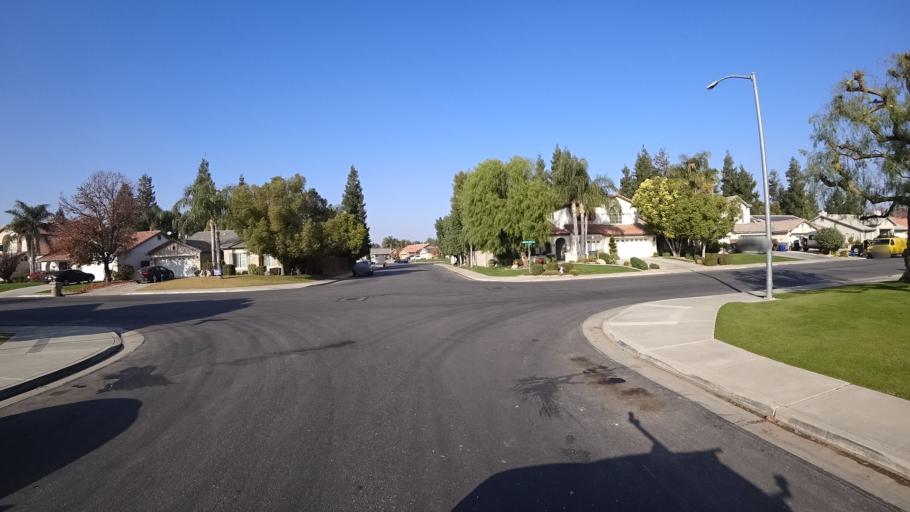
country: US
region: California
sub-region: Kern County
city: Greenacres
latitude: 35.4150
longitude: -119.0994
